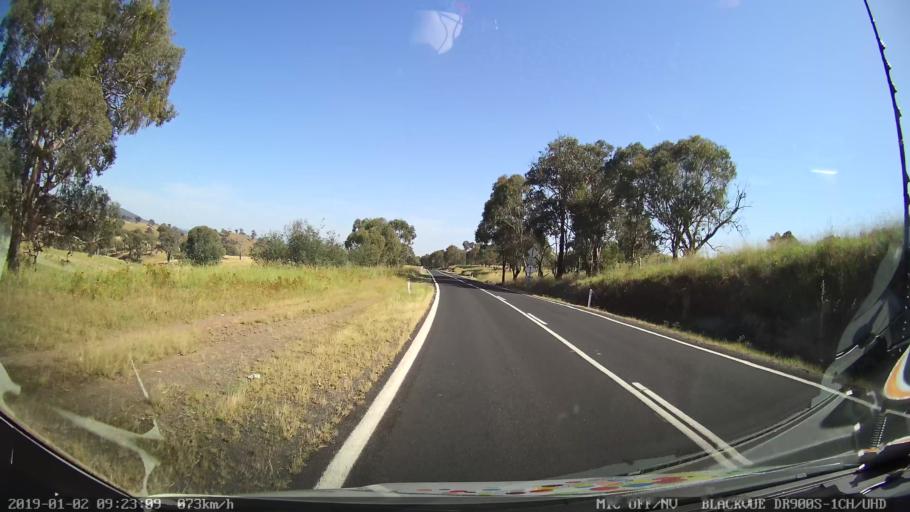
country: AU
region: New South Wales
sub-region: Tumut Shire
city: Tumut
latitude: -35.3906
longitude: 148.2981
